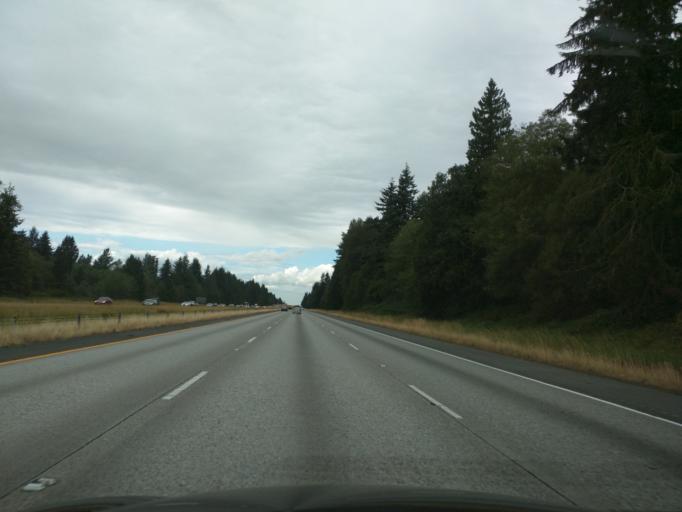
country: US
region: Washington
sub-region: Snohomish County
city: Stanwood
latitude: 48.2805
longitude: -122.2835
